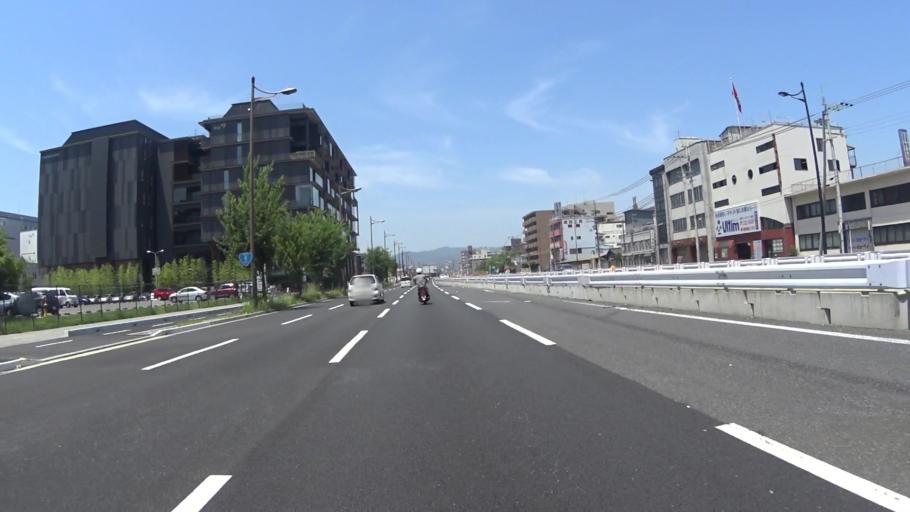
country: JP
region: Kyoto
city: Ayabe
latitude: 35.1609
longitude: 135.4263
